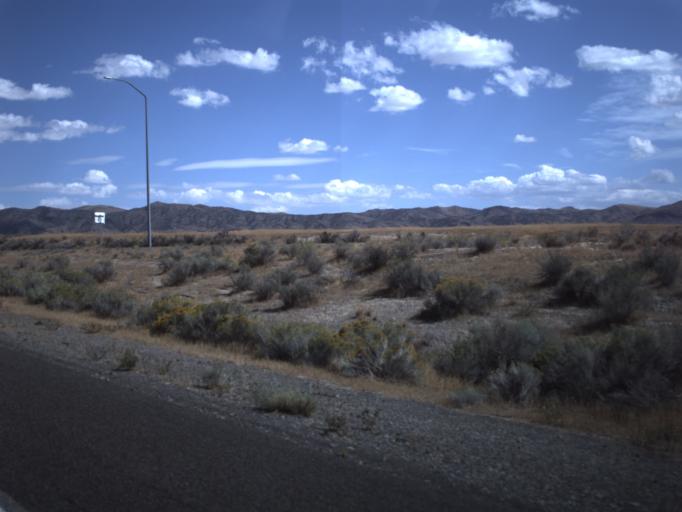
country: US
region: Utah
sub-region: Tooele County
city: Grantsville
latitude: 40.7583
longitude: -113.0163
